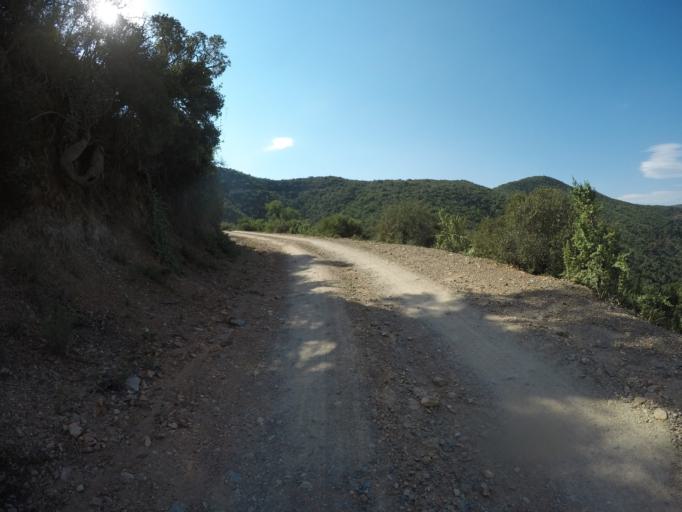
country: ZA
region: Eastern Cape
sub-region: Cacadu District Municipality
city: Kareedouw
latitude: -33.6531
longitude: 24.3486
